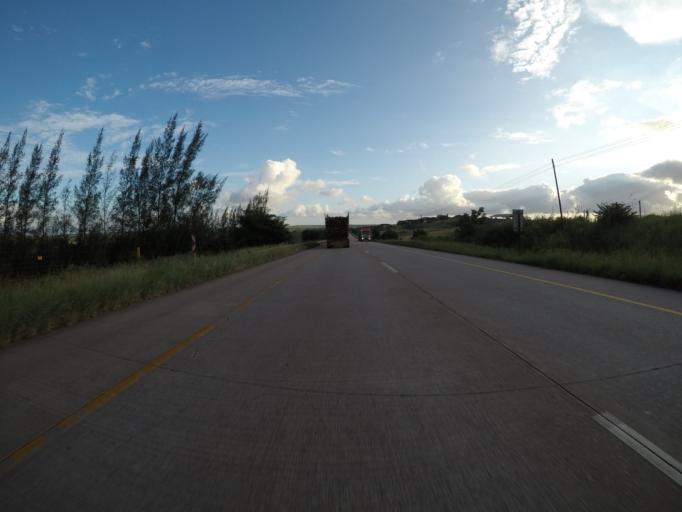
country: ZA
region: KwaZulu-Natal
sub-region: uMkhanyakude District Municipality
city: Mtubatuba
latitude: -28.4793
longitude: 32.1439
